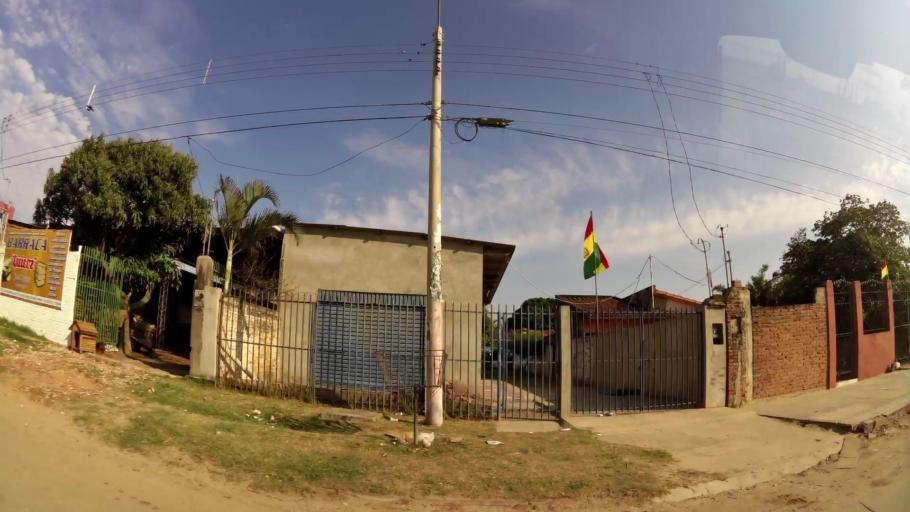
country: BO
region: Santa Cruz
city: Santa Cruz de la Sierra
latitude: -17.7291
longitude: -63.1376
